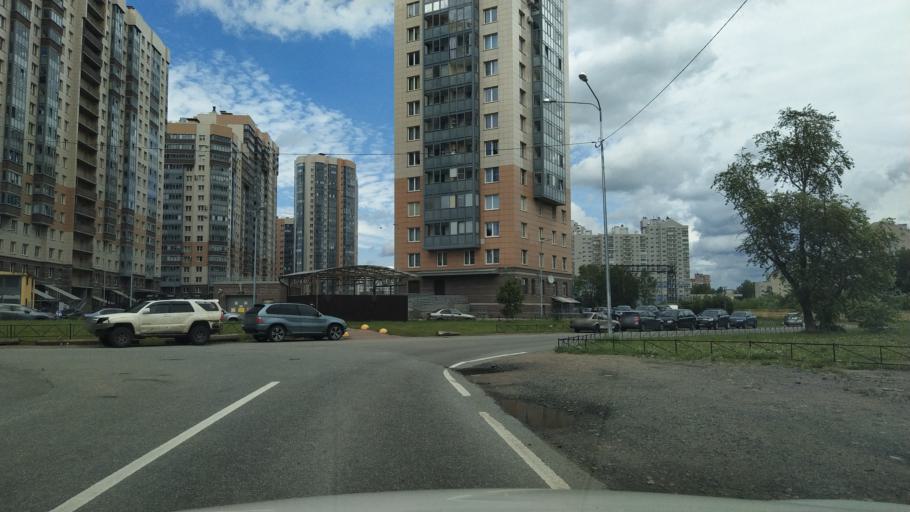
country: RU
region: Leningrad
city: Akademicheskoe
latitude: 60.0102
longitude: 30.3870
